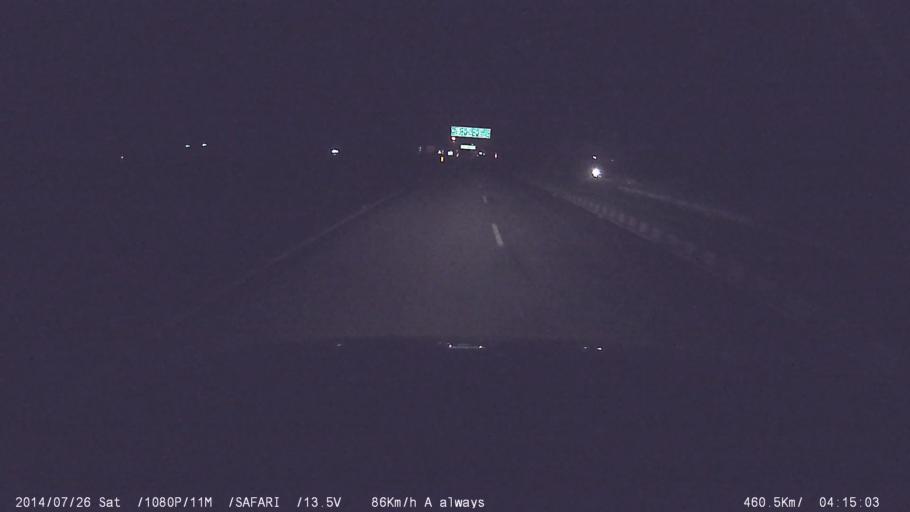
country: IN
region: Kerala
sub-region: Thrissur District
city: Trichur
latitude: 10.4573
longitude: 76.2581
